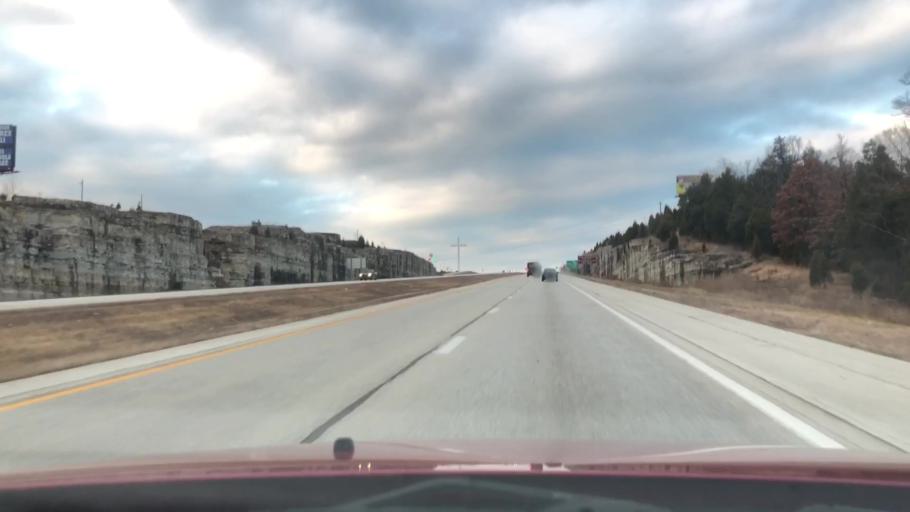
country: US
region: Missouri
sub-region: Taney County
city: Merriam Woods
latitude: 36.7400
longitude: -93.2216
